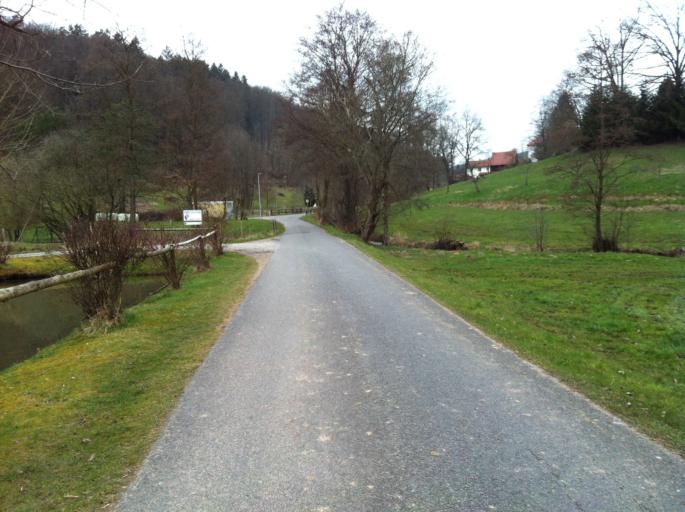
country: DE
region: Hesse
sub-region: Regierungsbezirk Darmstadt
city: Beerfelden
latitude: 49.6222
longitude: 8.9234
